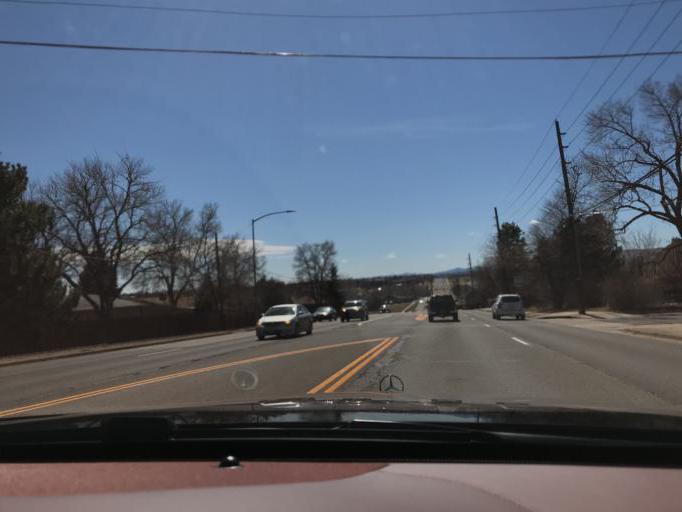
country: US
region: Colorado
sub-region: Jefferson County
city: Arvada
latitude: 39.8062
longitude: -105.1380
